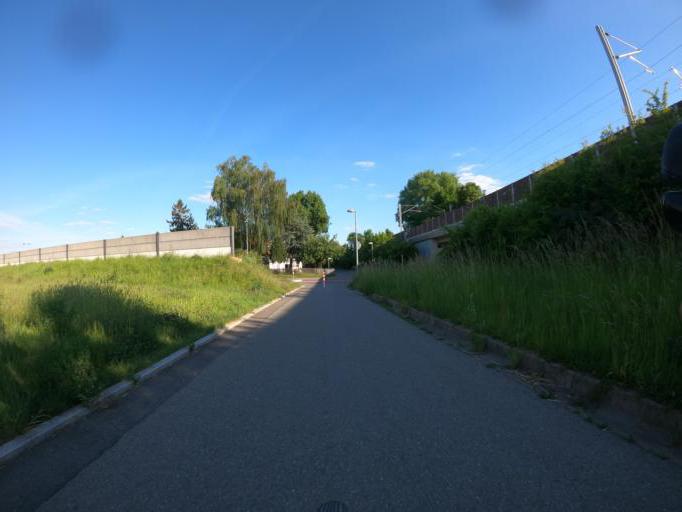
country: DE
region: Baden-Wuerttemberg
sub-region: Regierungsbezirk Stuttgart
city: Magstadt
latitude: 48.7191
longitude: 8.9700
